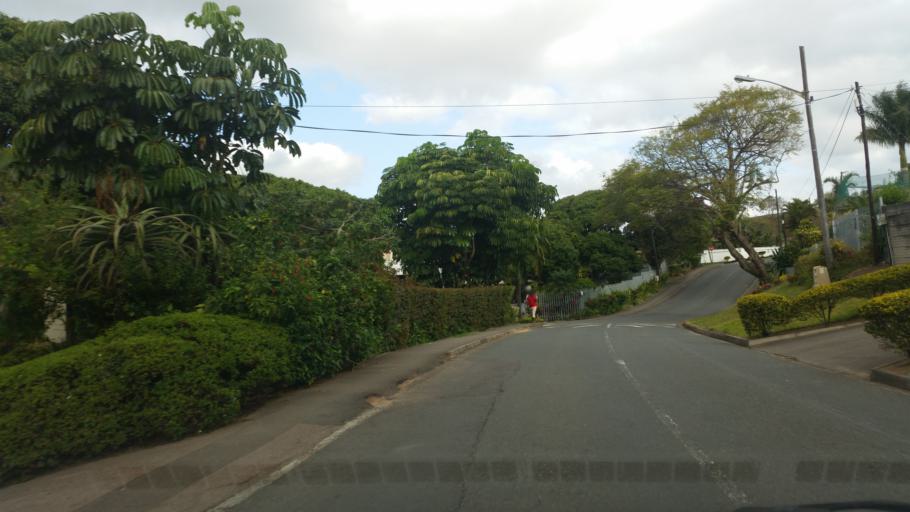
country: ZA
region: KwaZulu-Natal
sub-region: eThekwini Metropolitan Municipality
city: Berea
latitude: -29.8288
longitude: 30.9413
